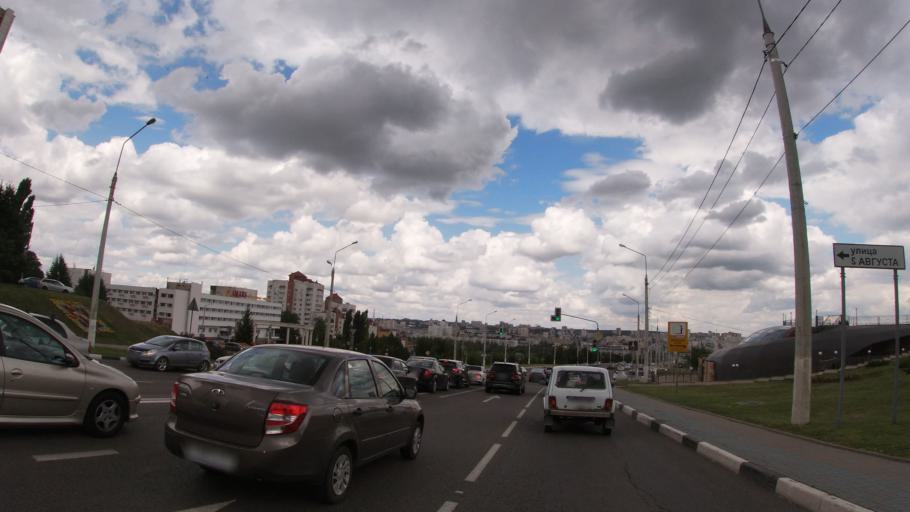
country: RU
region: Belgorod
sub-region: Belgorodskiy Rayon
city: Belgorod
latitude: 50.5804
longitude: 36.5829
